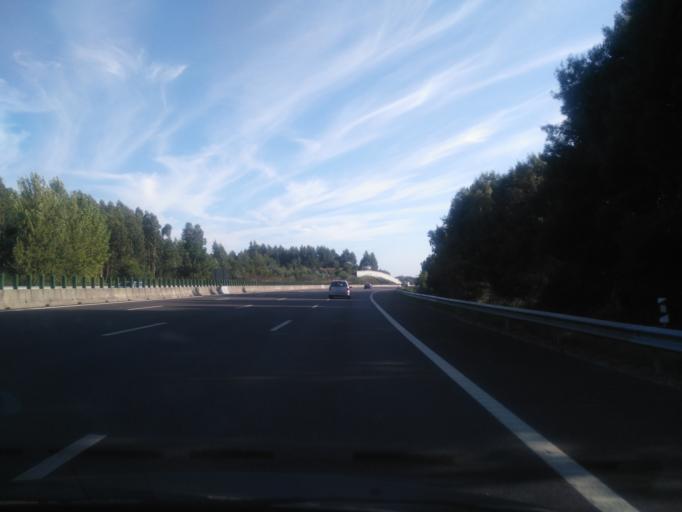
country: PT
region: Porto
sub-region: Vila Nova de Gaia
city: Grijo
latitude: 41.0399
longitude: -8.5701
